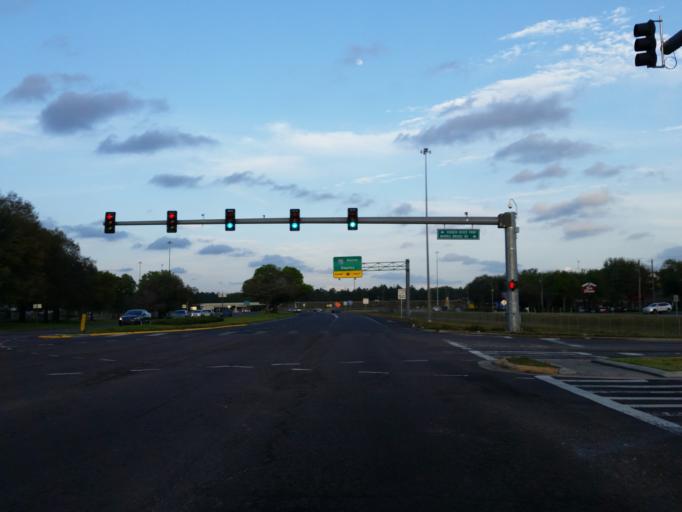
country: US
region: Florida
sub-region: Hillsborough County
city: Temple Terrace
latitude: 28.0691
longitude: -82.3598
